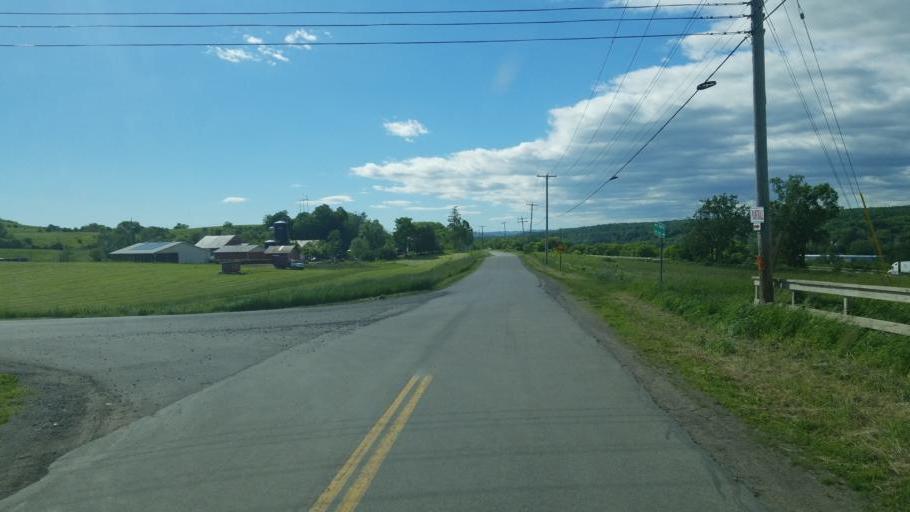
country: US
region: New York
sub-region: Montgomery County
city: Saint Johnsville
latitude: 42.9873
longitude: -74.6693
